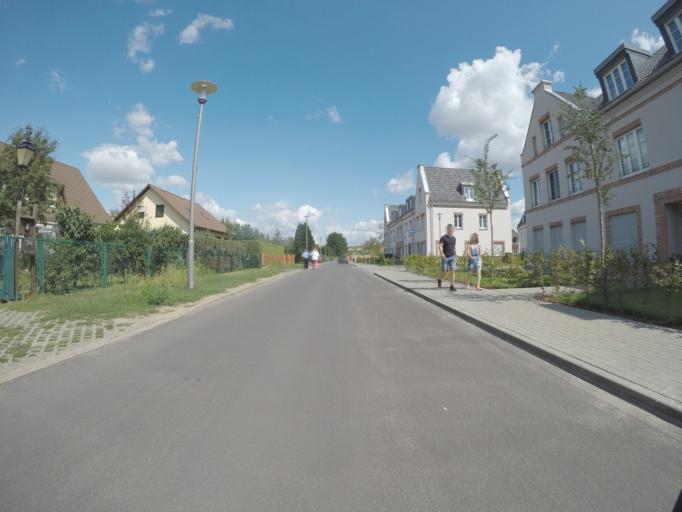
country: DE
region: Berlin
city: Kaulsdorf
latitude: 52.5038
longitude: 13.5762
